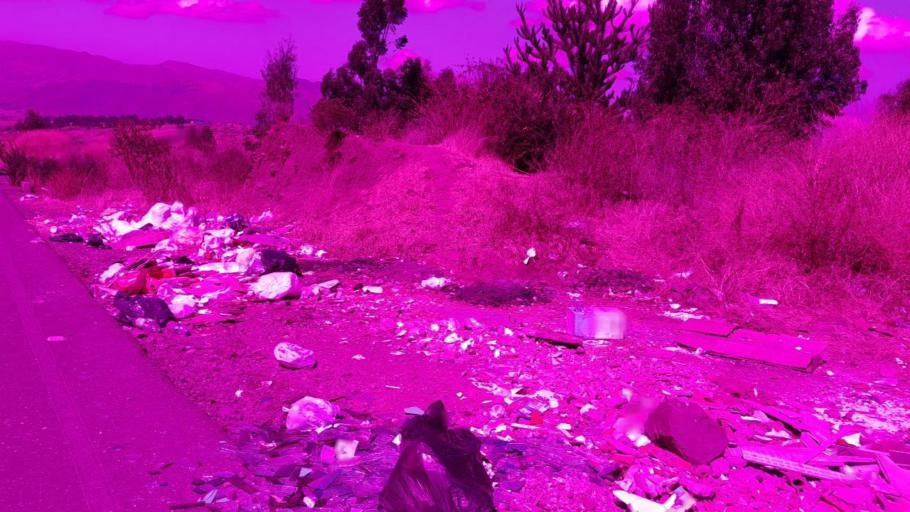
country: PE
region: Cusco
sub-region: Provincia de Cusco
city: Cusco
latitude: -13.4983
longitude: -71.9273
